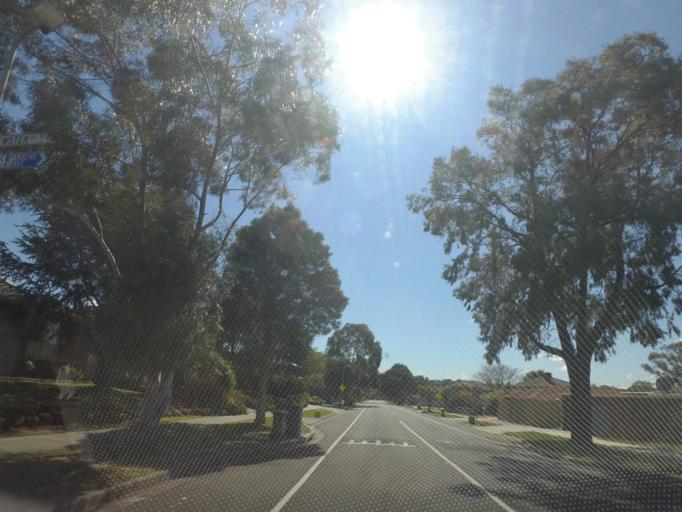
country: AU
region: Victoria
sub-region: Knox
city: Wantirna South
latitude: -37.8836
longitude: 145.2240
